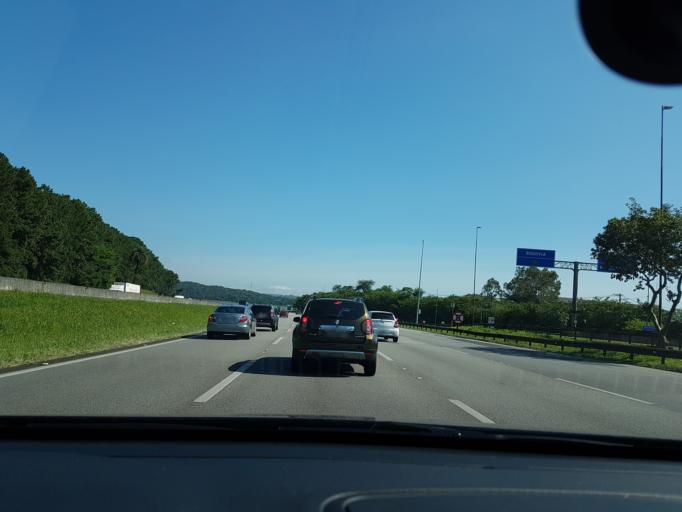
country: BR
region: Sao Paulo
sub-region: Sao Bernardo Do Campo
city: Sao Bernardo do Campo
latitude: -23.7841
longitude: -46.5981
